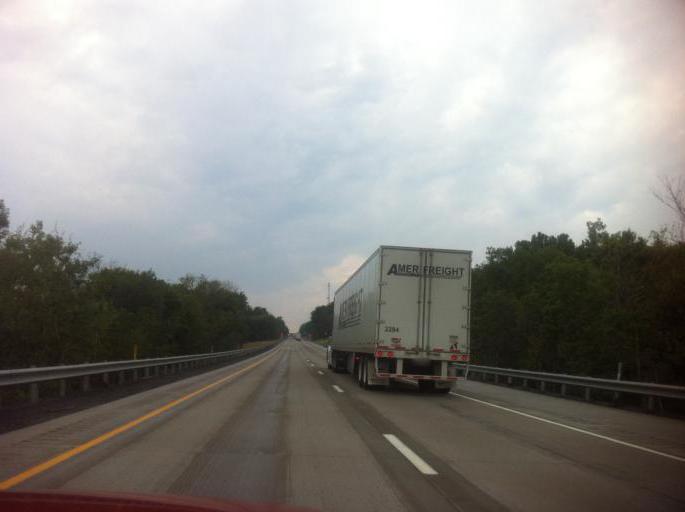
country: US
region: Pennsylvania
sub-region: Jefferson County
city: Falls Creek
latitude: 41.1498
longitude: -78.8575
